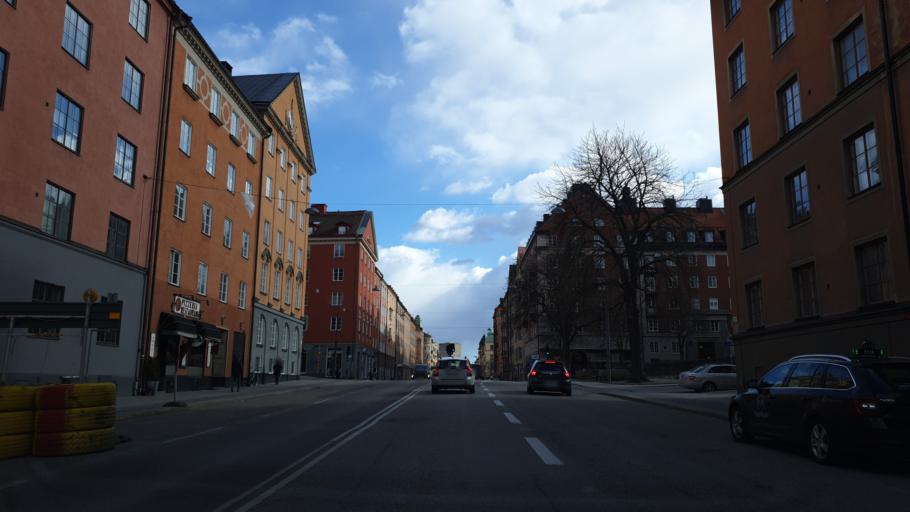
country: SE
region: Stockholm
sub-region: Stockholms Kommun
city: Stockholm
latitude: 59.3447
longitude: 18.0348
